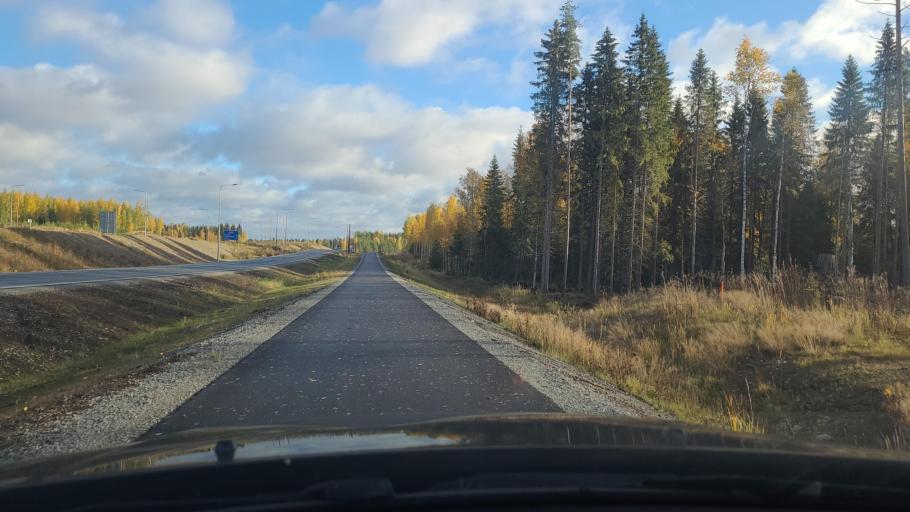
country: FI
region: Southern Savonia
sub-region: Pieksaemaeki
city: Juva
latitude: 61.8814
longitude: 27.7804
